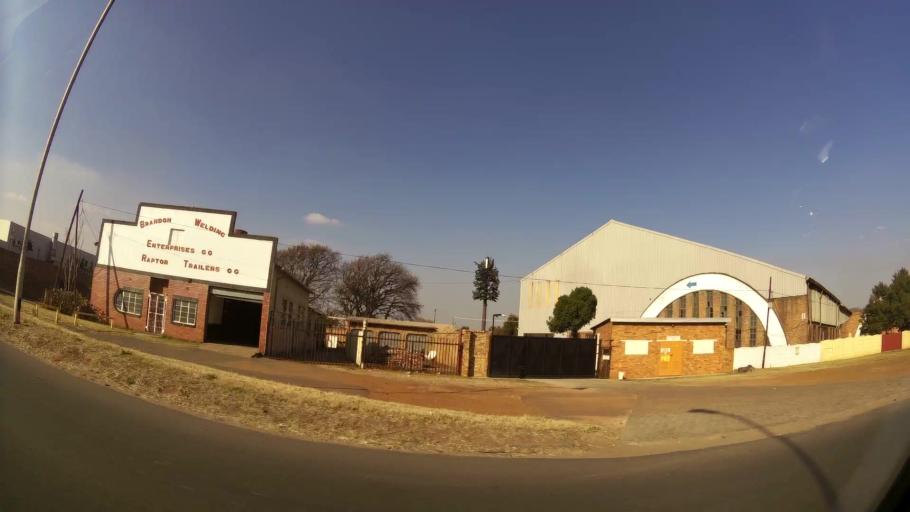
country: ZA
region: Gauteng
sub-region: Ekurhuleni Metropolitan Municipality
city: Brakpan
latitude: -26.2254
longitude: 28.3596
